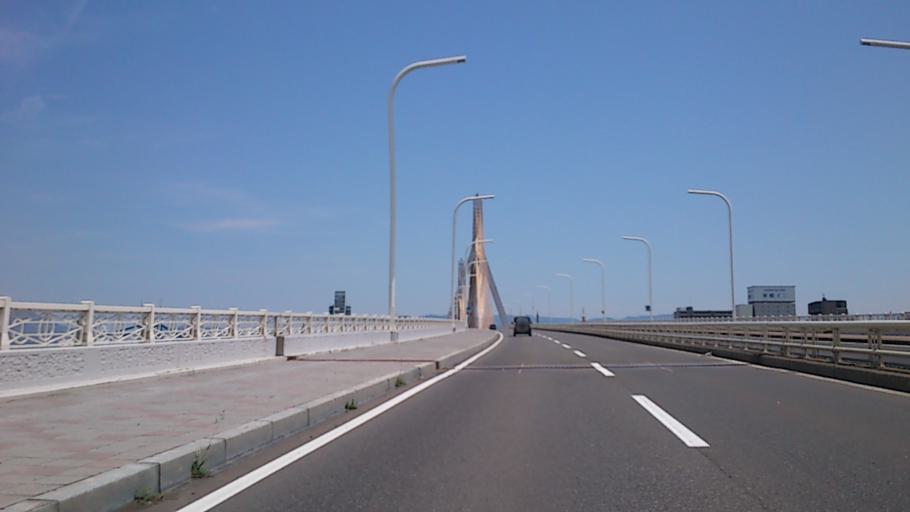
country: JP
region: Aomori
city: Aomori Shi
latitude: 40.8321
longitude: 140.7312
